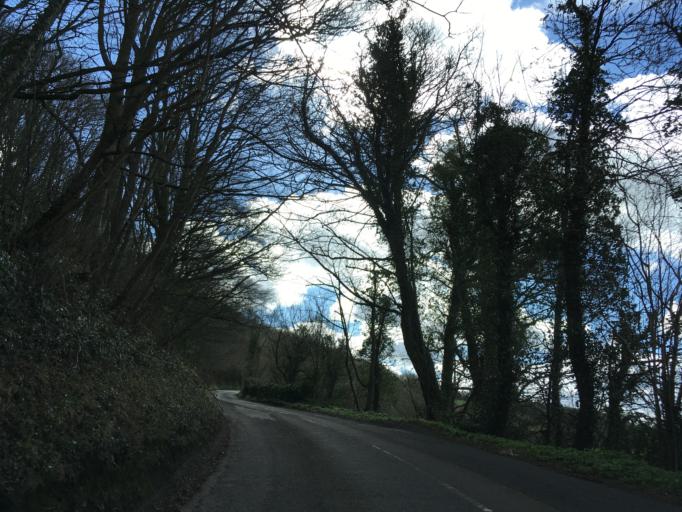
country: GB
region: England
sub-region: Gloucestershire
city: Wotton-under-Edge
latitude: 51.5972
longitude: -2.3352
